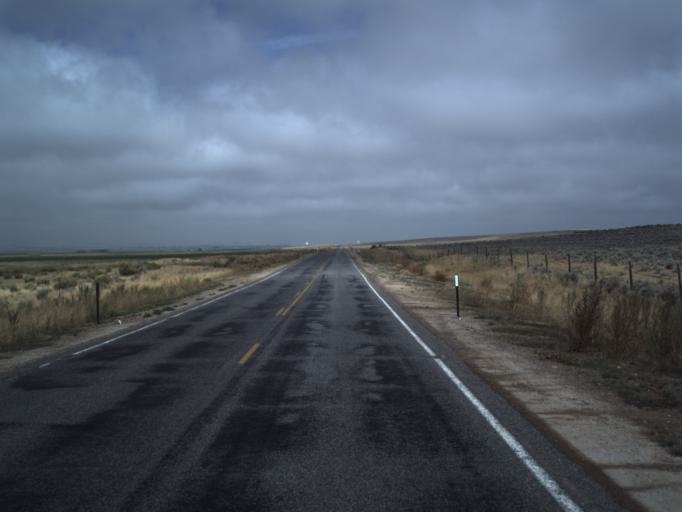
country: US
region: Utah
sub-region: Rich County
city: Randolph
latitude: 41.4660
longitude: -111.1034
